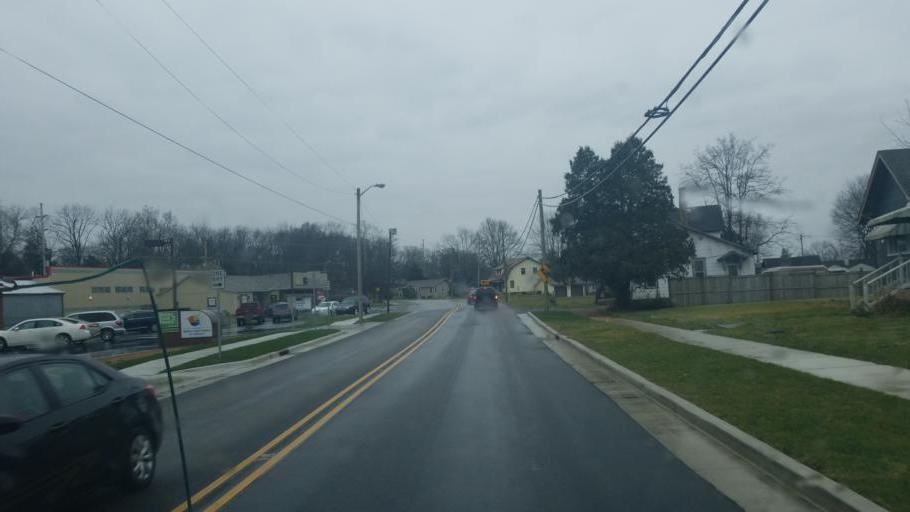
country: US
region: Indiana
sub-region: Shelby County
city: Shelbyville
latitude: 39.5114
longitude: -85.7740
